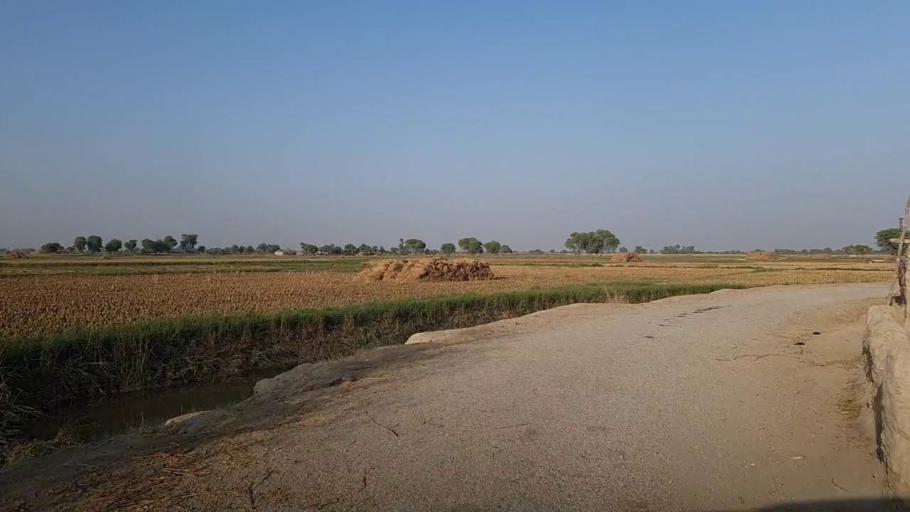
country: PK
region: Sindh
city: Kashmor
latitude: 28.4245
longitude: 69.4272
